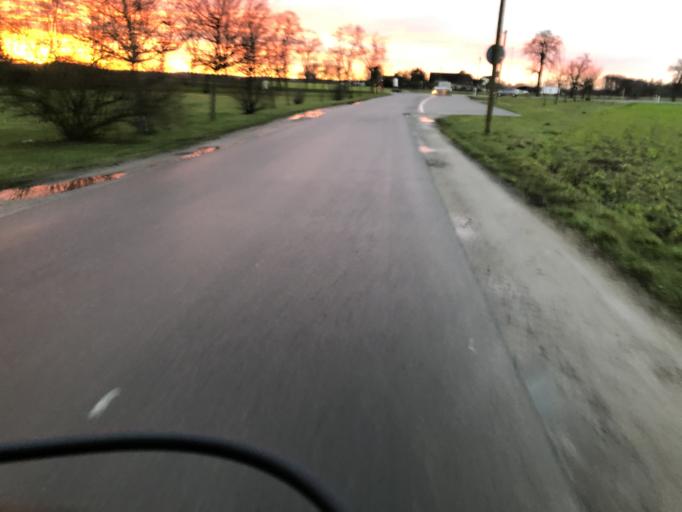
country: DE
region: Baden-Wuerttemberg
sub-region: Karlsruhe Region
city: Reilingen
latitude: 49.2954
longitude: 8.5814
